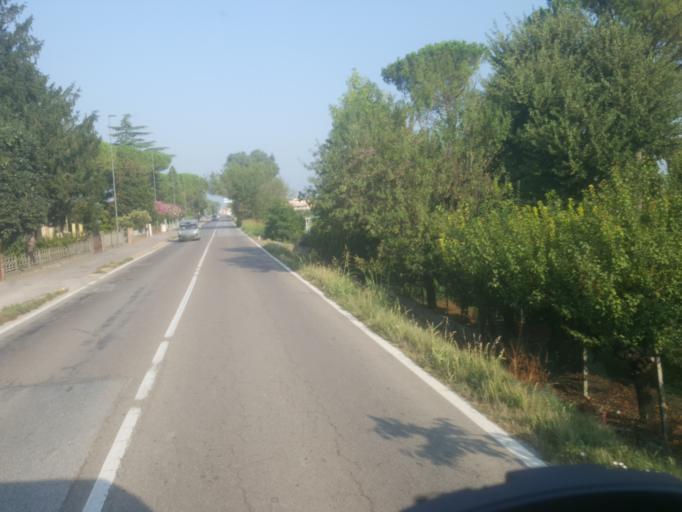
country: IT
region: Emilia-Romagna
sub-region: Provincia di Ravenna
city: Mezzano
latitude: 44.4621
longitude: 12.0949
